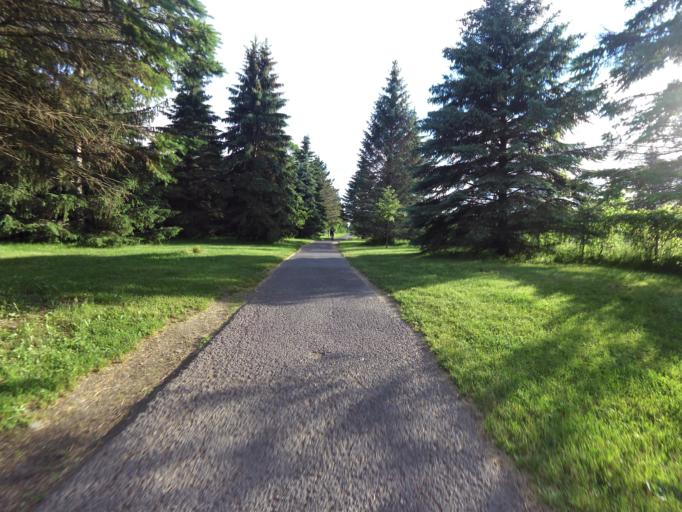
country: CA
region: Ontario
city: Bells Corners
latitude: 45.2675
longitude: -75.7615
